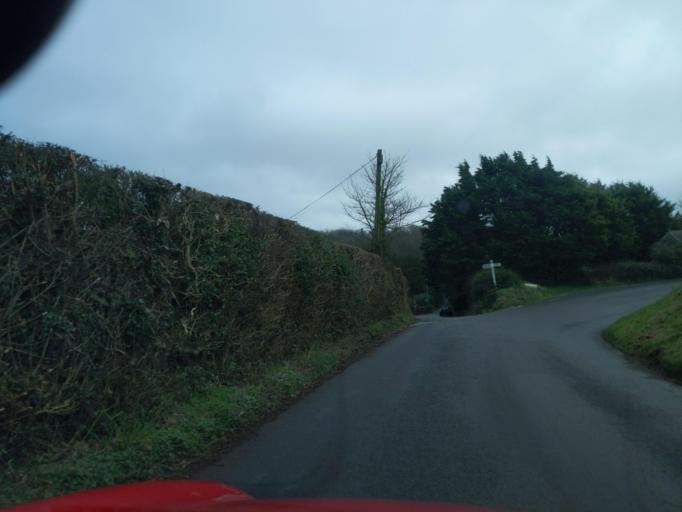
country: GB
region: England
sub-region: Devon
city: Wembury
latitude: 50.3288
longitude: -4.0917
